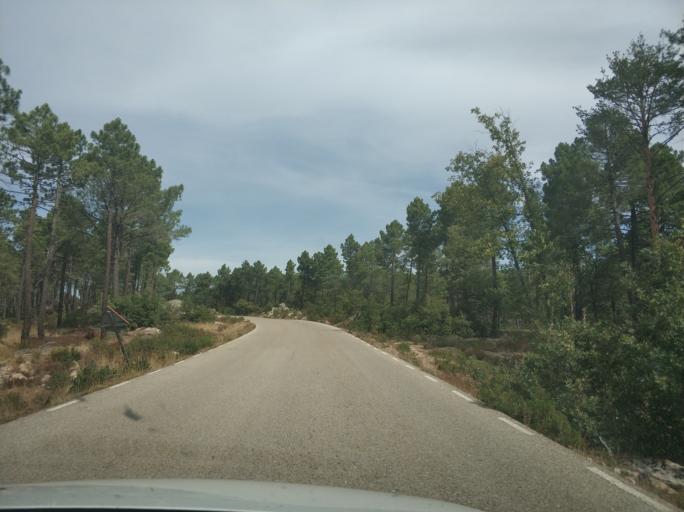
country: ES
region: Castille and Leon
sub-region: Provincia de Soria
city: Duruelo de la Sierra
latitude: 41.8853
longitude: -2.9374
